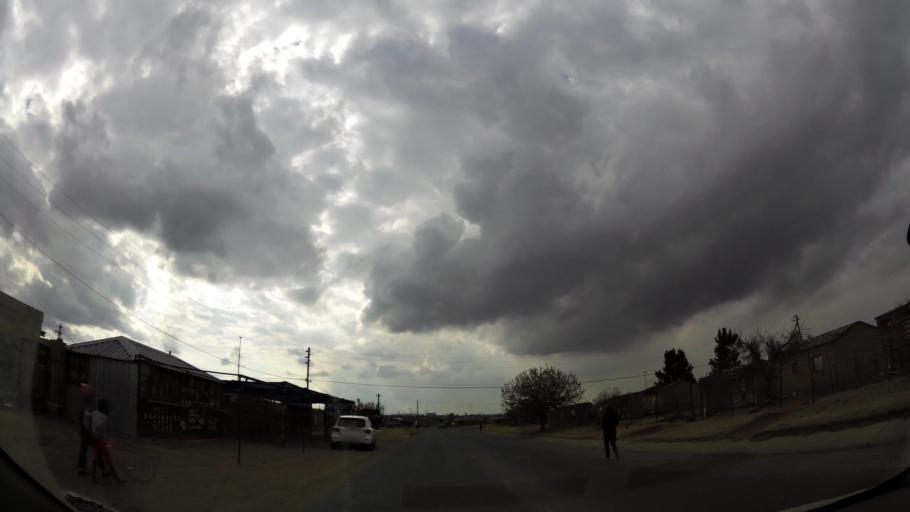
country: ZA
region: Orange Free State
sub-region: Fezile Dabi District Municipality
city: Sasolburg
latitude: -26.8564
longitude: 27.8528
